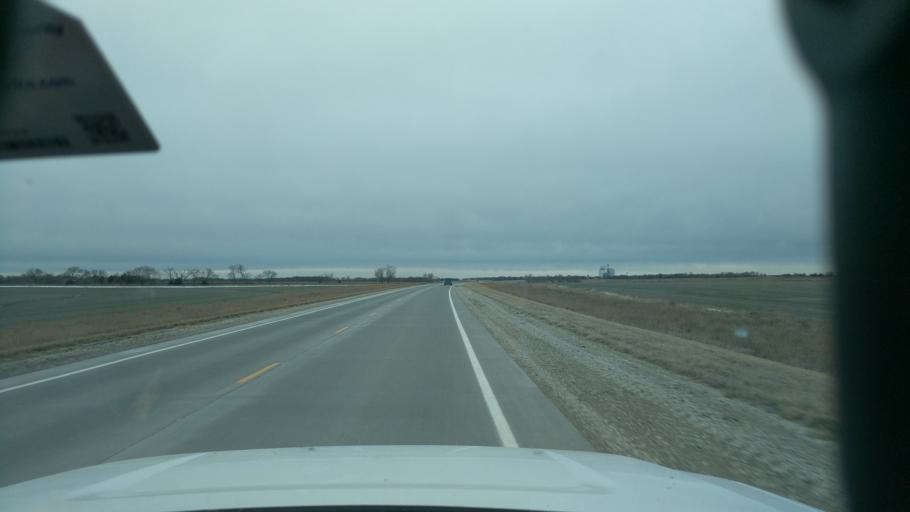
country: US
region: Kansas
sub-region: Dickinson County
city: Herington
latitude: 38.5186
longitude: -96.9562
